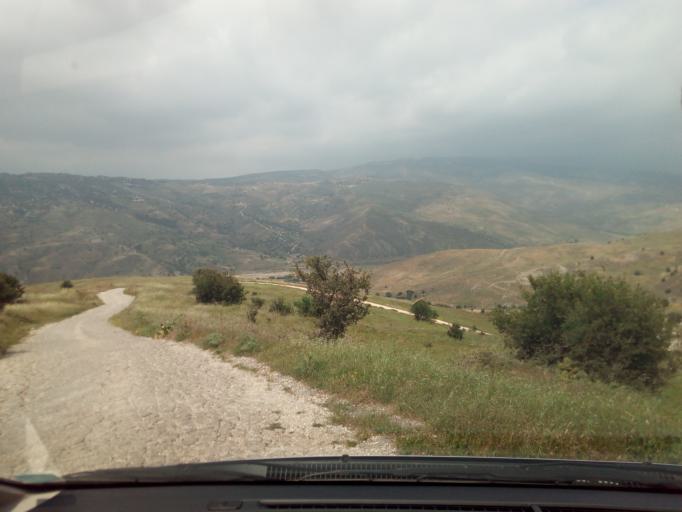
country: CY
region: Limassol
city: Pachna
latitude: 34.8158
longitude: 32.6411
